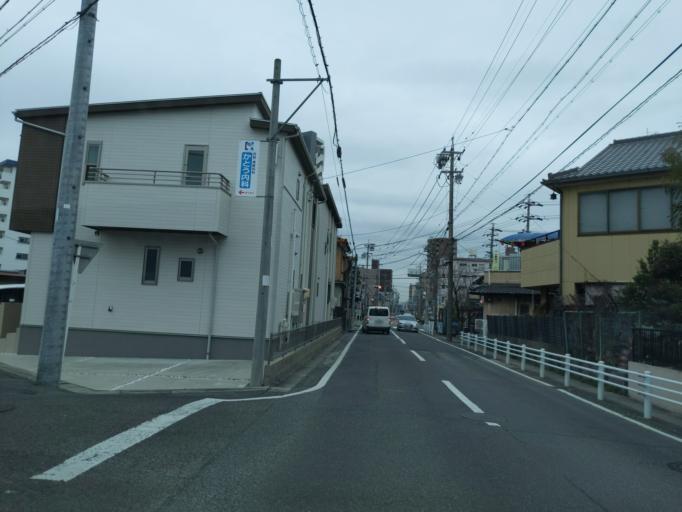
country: JP
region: Aichi
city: Kasugai
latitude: 35.2462
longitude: 136.9878
